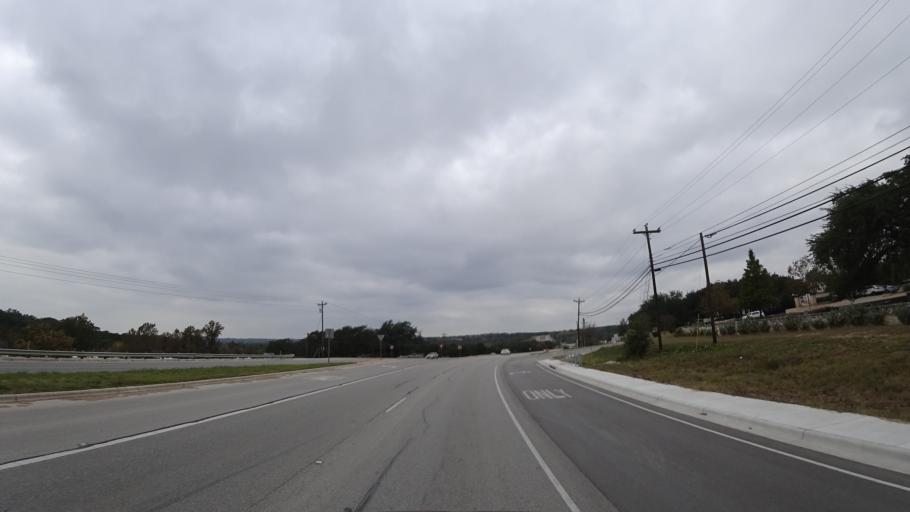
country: US
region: Texas
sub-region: Williamson County
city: Anderson Mill
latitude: 30.4575
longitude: -97.8336
